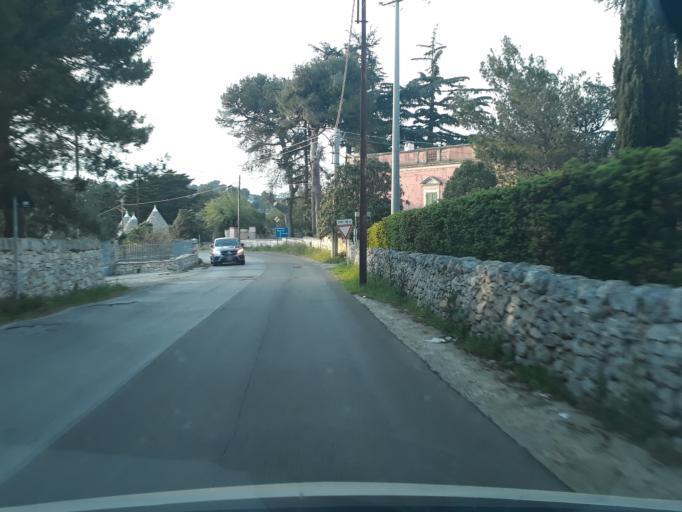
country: IT
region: Apulia
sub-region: Provincia di Brindisi
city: Lamie di Olimpie-Selva
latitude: 40.7985
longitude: 17.3539
